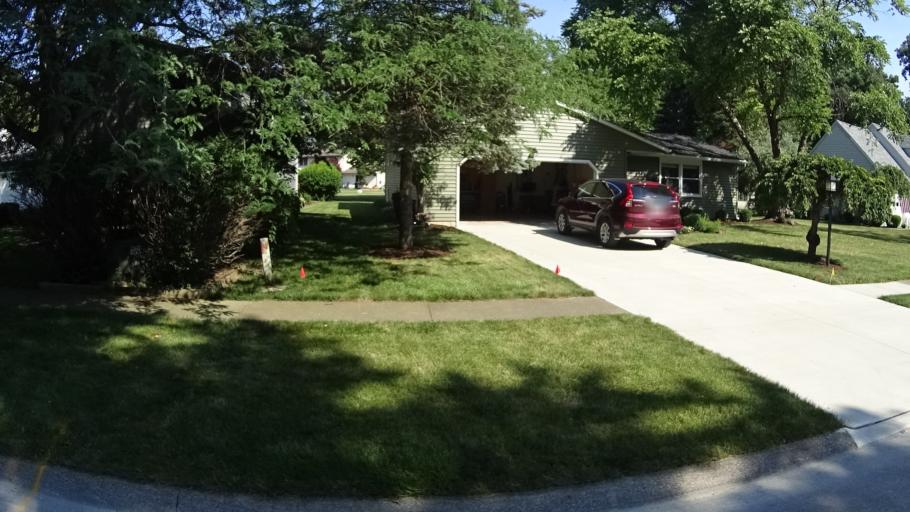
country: US
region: Ohio
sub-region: Erie County
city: Huron
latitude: 41.3990
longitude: -82.5709
